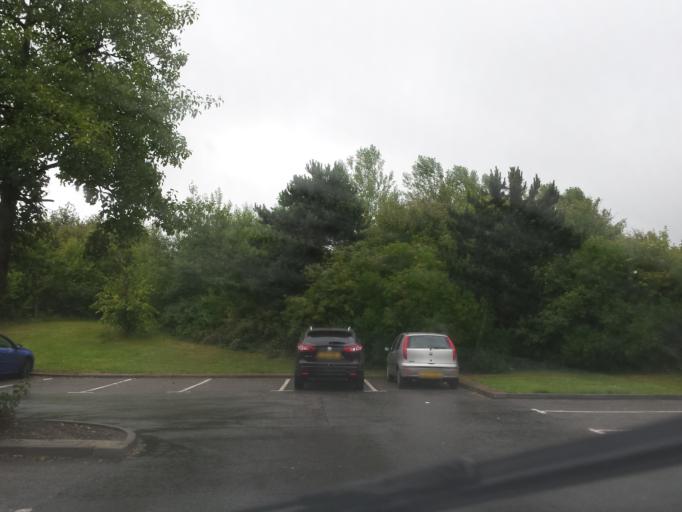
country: GB
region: England
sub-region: Derbyshire
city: Tibshelf
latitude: 53.1399
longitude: -1.3285
